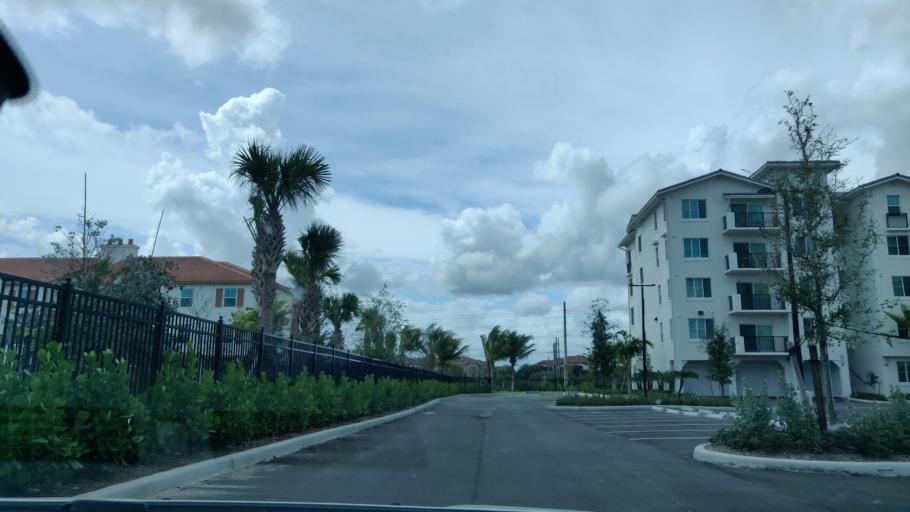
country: US
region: Florida
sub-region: Miami-Dade County
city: Country Club
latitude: 25.9812
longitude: -80.2978
